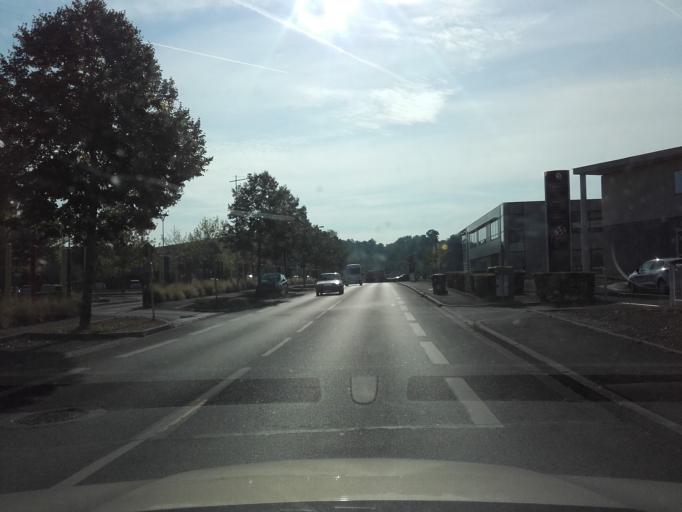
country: FR
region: Centre
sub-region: Departement d'Indre-et-Loire
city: Joue-les-Tours
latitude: 47.3651
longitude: 0.6754
